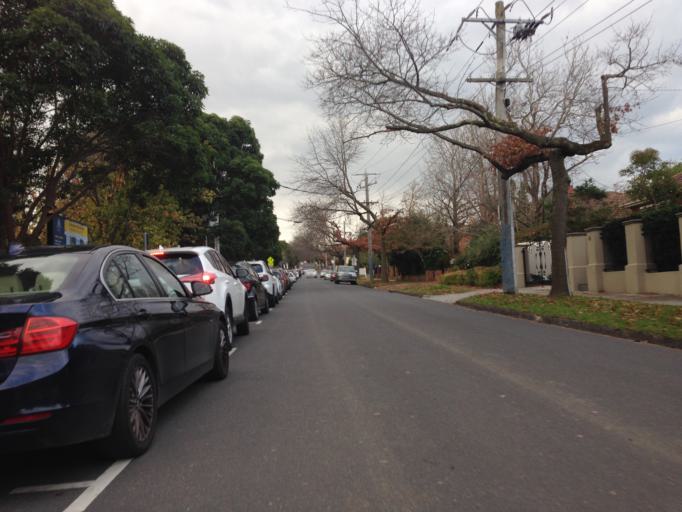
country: AU
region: Victoria
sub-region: Boroondara
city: Balwyn North
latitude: -37.7981
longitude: 145.0770
